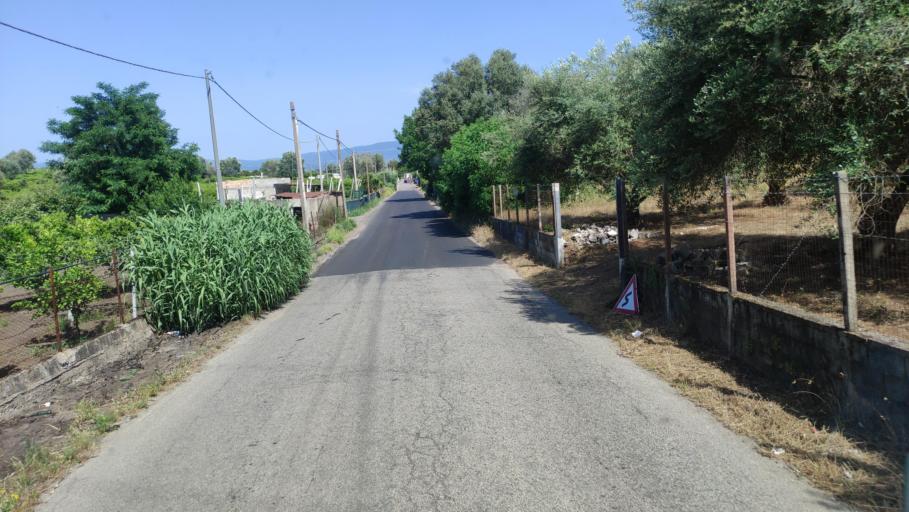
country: IT
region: Calabria
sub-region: Provincia di Reggio Calabria
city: Rosarno
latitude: 38.4550
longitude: 15.9768
